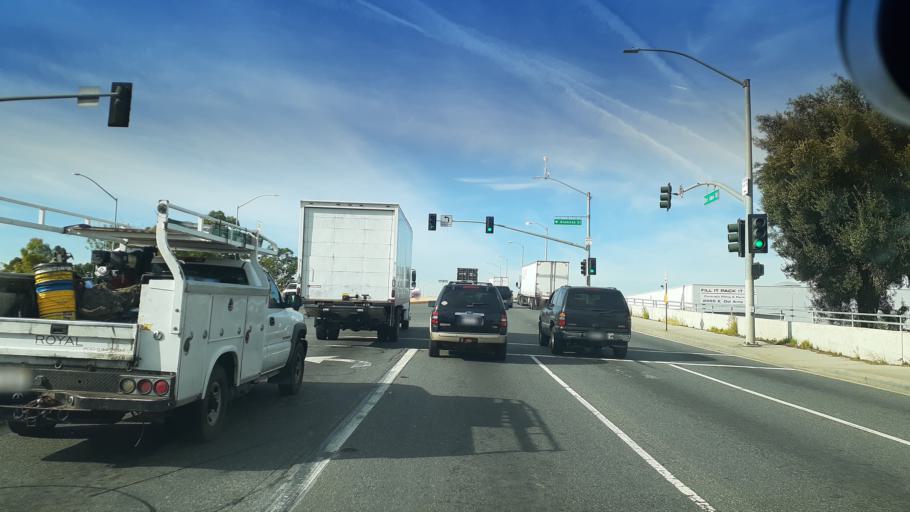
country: US
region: California
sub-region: Los Angeles County
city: Compton
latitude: 33.8467
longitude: -118.2175
